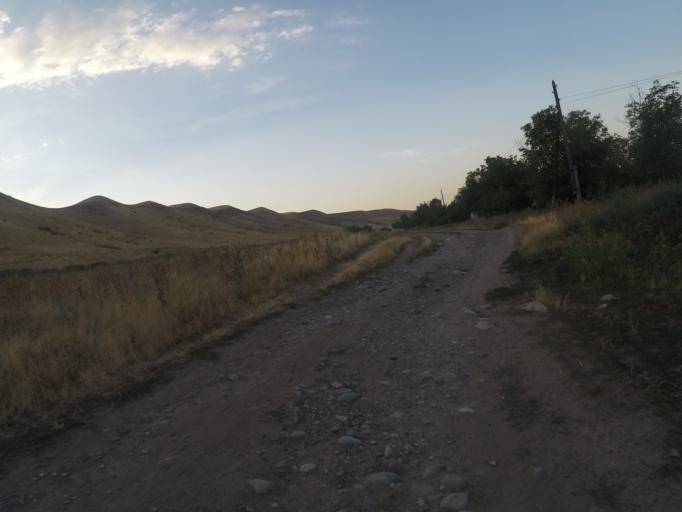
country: KG
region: Chuy
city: Bishkek
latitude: 42.7671
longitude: 74.6385
